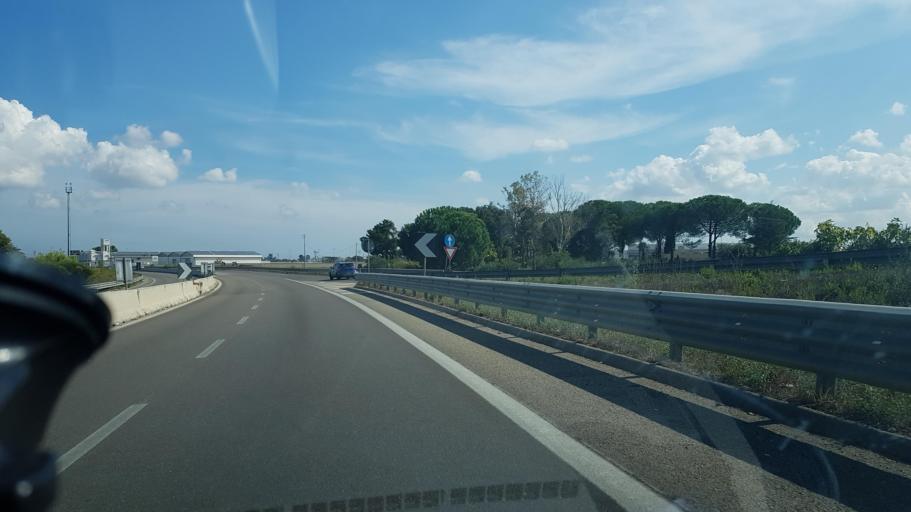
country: IT
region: Apulia
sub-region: Provincia di Brindisi
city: Mesagne
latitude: 40.5685
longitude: 17.8212
